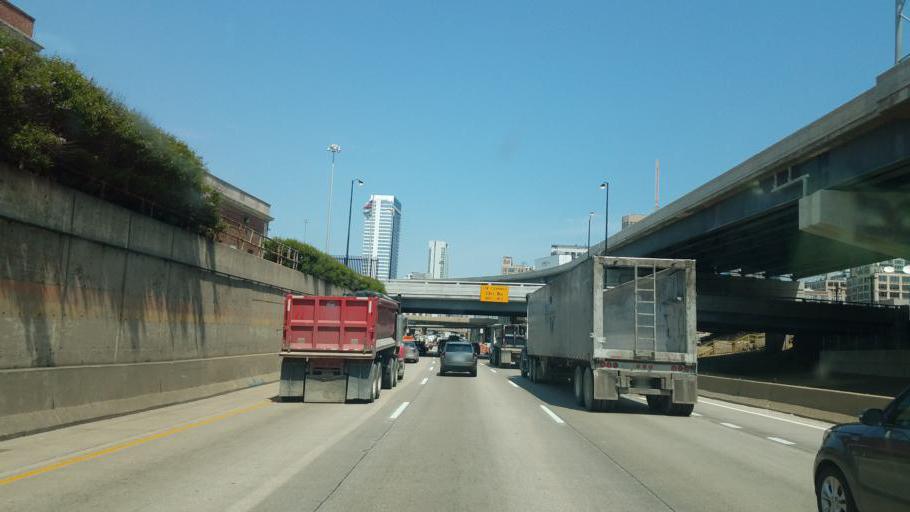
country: US
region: Illinois
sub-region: Cook County
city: Chicago
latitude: 41.8735
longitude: -87.6449
